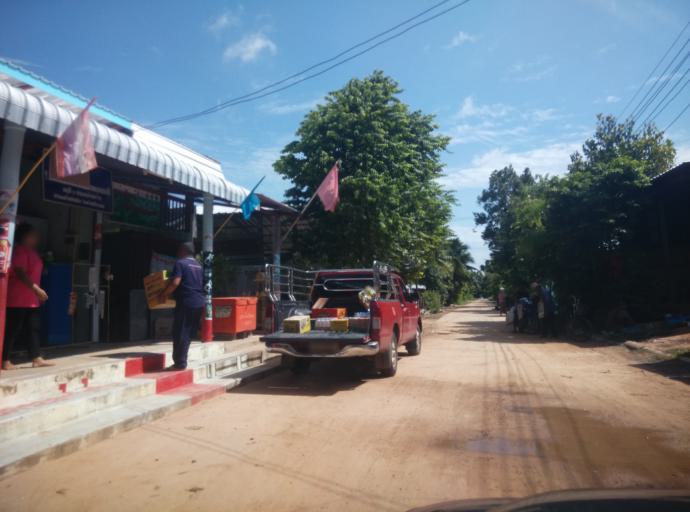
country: TH
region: Sisaket
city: Huai Thap Than
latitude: 14.9765
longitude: 104.0520
